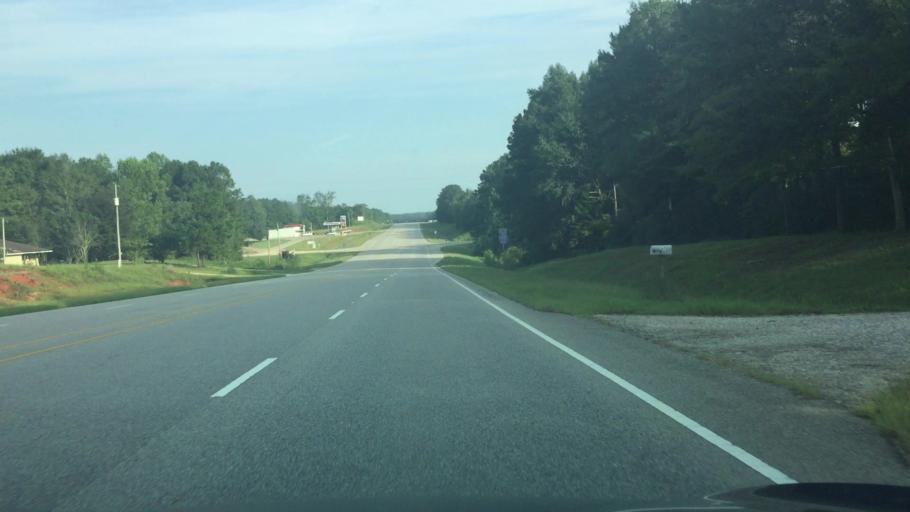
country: US
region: Alabama
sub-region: Butler County
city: Georgiana
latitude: 31.4856
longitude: -86.6804
